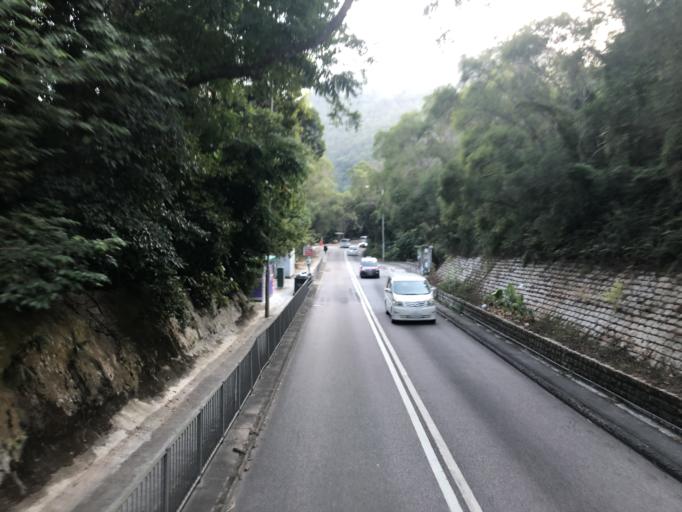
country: HK
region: Sai Kung
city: Sai Kung
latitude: 22.4182
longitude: 114.2661
